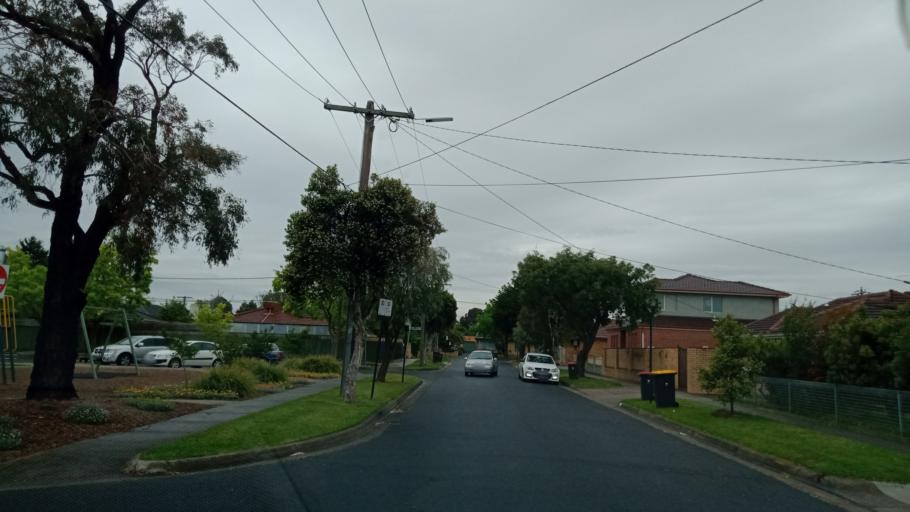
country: AU
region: Victoria
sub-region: Greater Dandenong
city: Springvale
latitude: -37.9332
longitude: 145.1617
